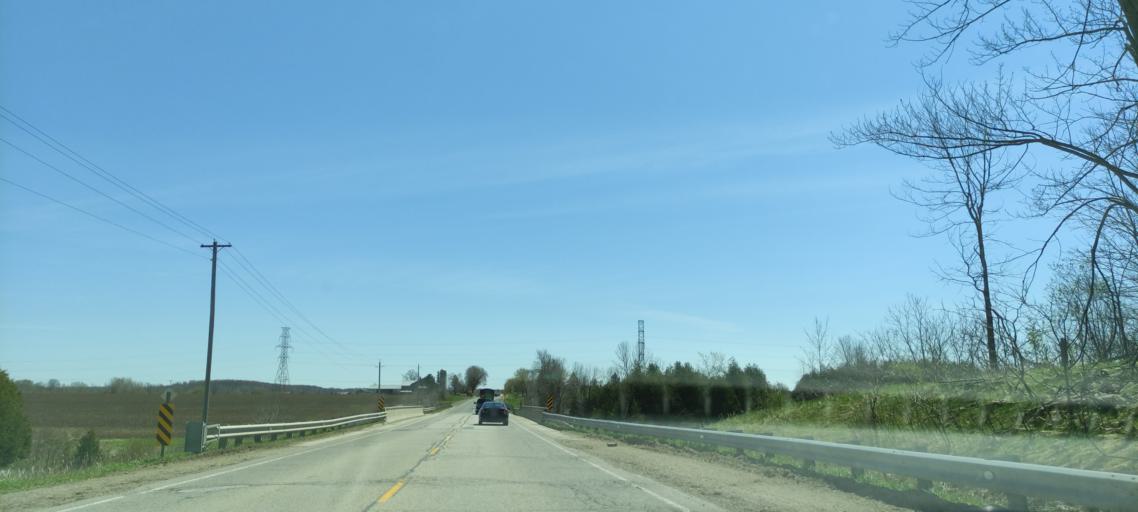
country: CA
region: Ontario
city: Waterloo
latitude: 43.5846
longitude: -80.4474
